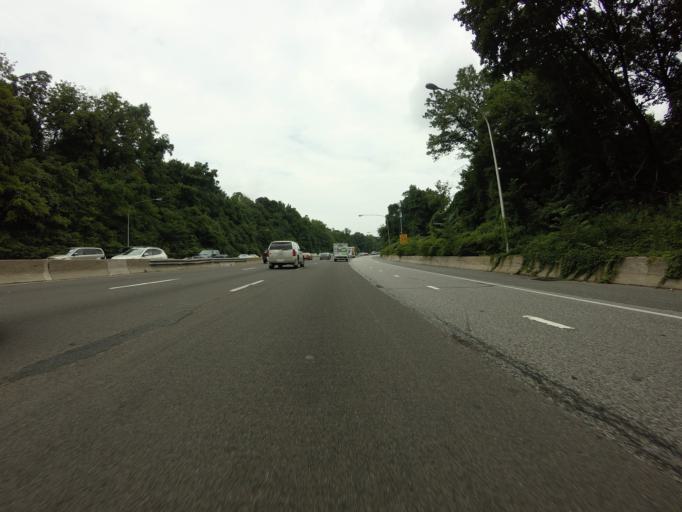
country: US
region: Pennsylvania
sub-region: Montgomery County
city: Bala-Cynwyd
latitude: 39.9828
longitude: -75.2078
